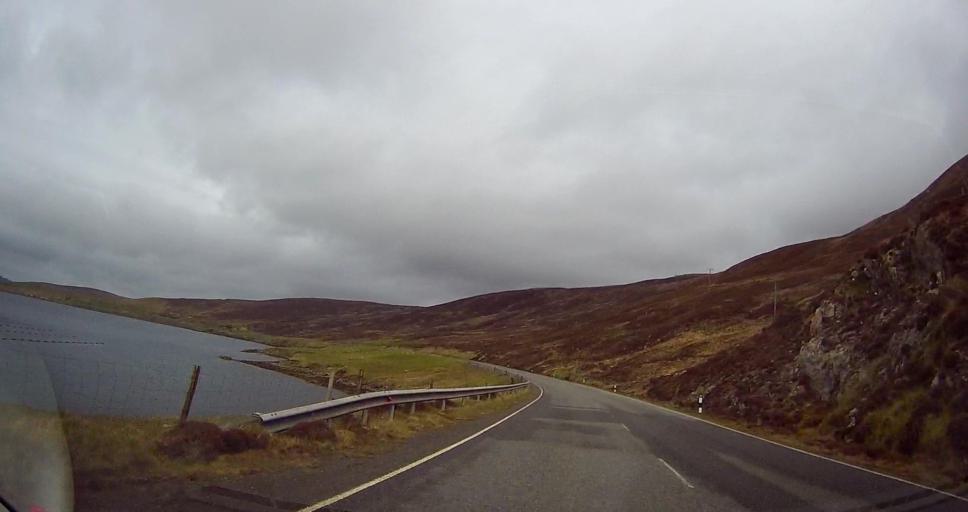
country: GB
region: Scotland
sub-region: Shetland Islands
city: Lerwick
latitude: 60.3616
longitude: -1.2859
